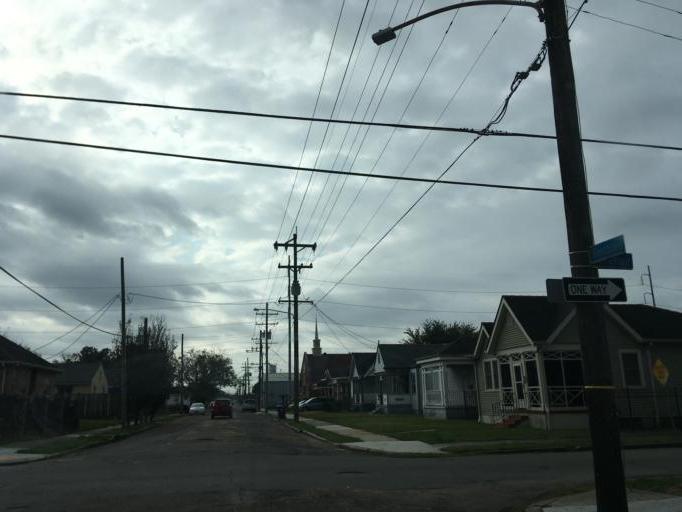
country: US
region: Louisiana
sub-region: Orleans Parish
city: New Orleans
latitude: 29.9899
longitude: -90.0599
